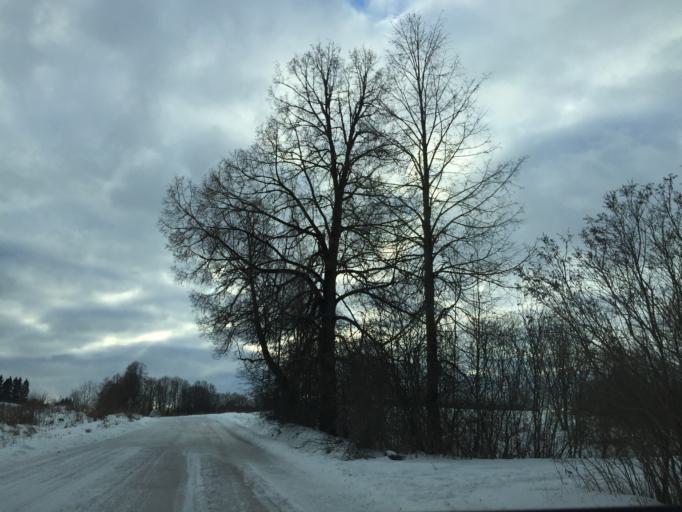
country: LV
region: Lielvarde
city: Lielvarde
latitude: 56.5804
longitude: 24.7352
